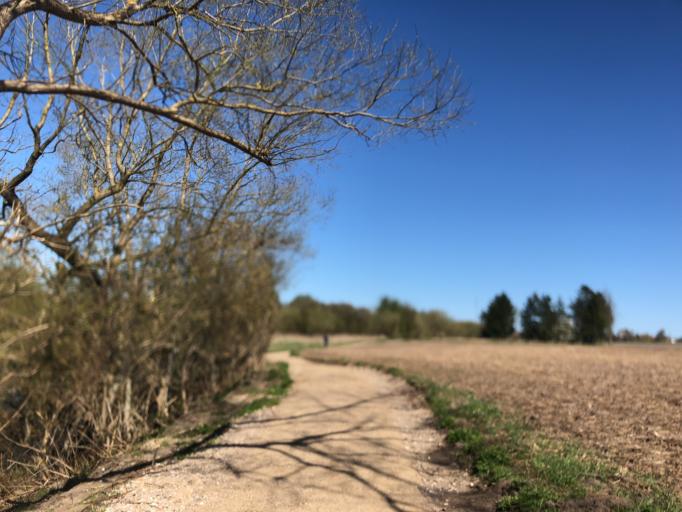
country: DK
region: Zealand
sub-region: Ringsted Kommune
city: Ringsted
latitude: 55.4274
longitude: 11.7751
